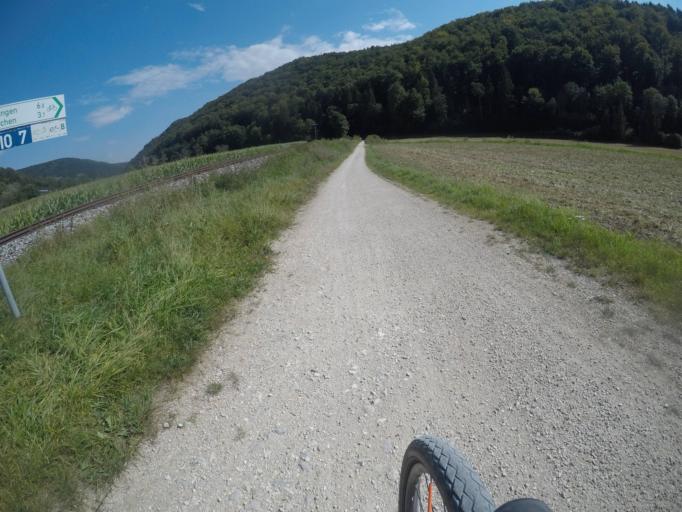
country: DE
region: Baden-Wuerttemberg
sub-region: Tuebingen Region
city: Schelklingen
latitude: 48.3661
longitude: 9.6702
